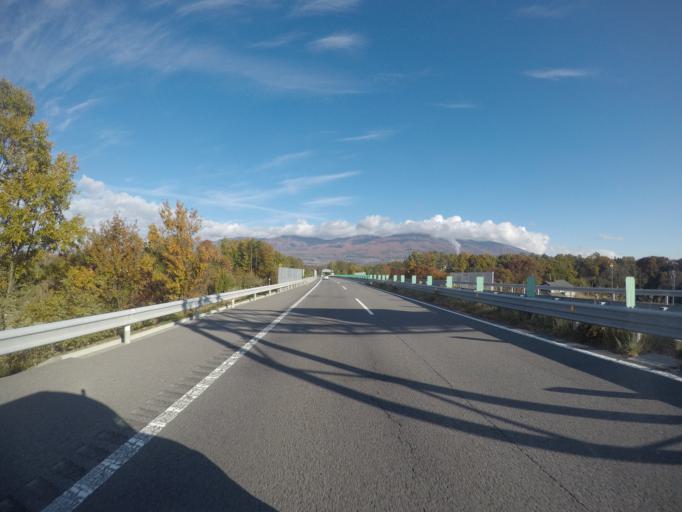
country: JP
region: Nagano
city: Komoro
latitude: 36.3084
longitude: 138.4809
